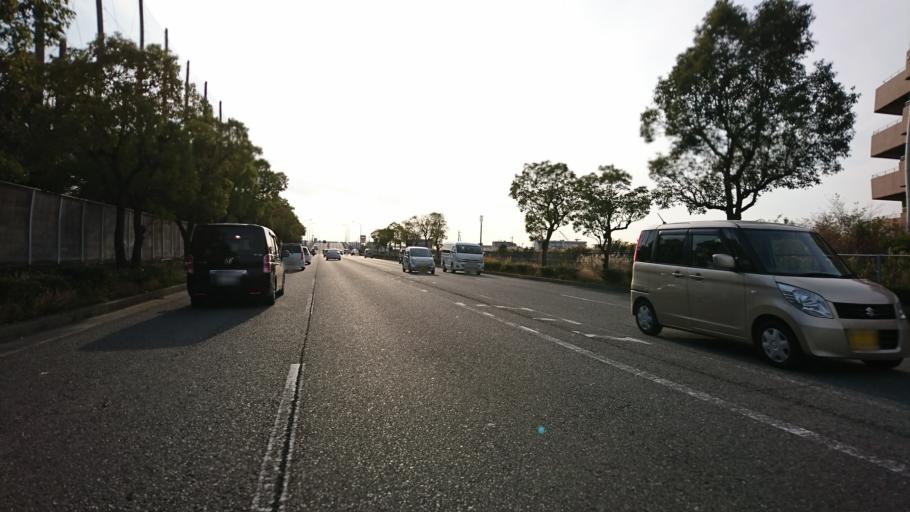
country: JP
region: Hyogo
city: Kakogawacho-honmachi
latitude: 34.7088
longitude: 134.8806
